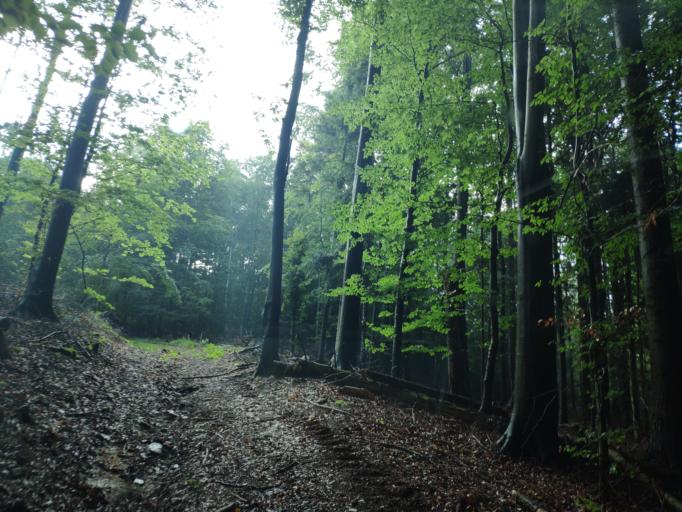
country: SK
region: Kosicky
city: Medzev
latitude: 48.7495
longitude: 20.9912
